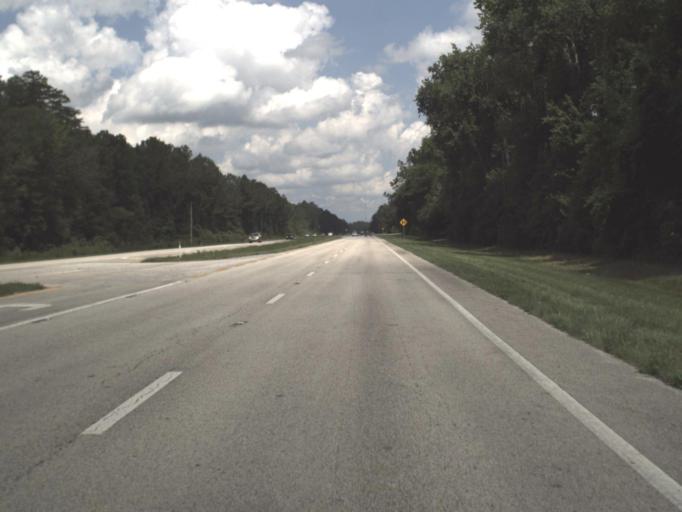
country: US
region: Florida
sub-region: Alachua County
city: Alachua
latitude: 29.7192
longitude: -82.3623
